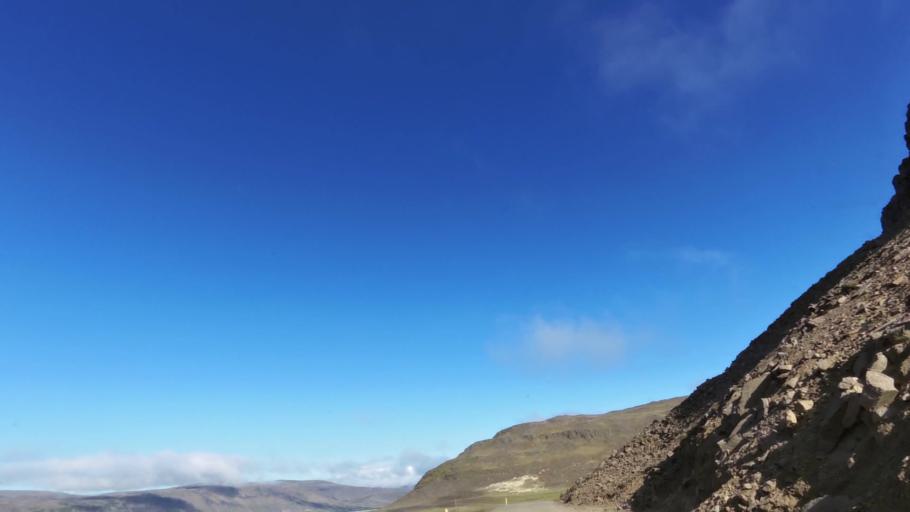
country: IS
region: West
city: Olafsvik
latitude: 65.5610
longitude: -24.0212
